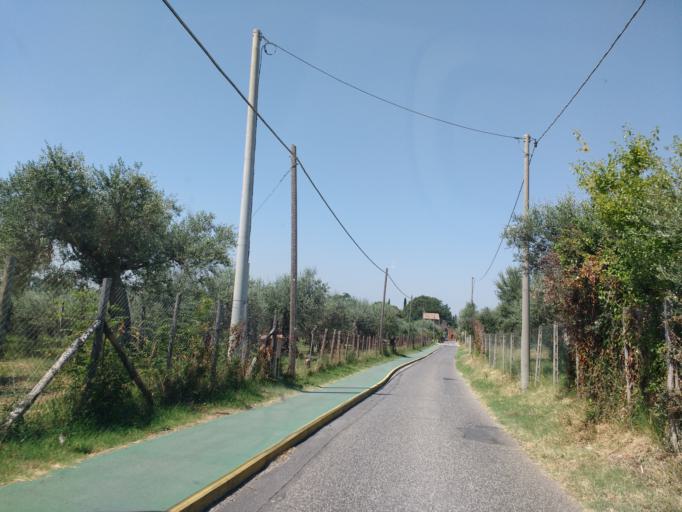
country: IT
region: Latium
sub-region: Citta metropolitana di Roma Capitale
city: Villa Adriana
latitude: 41.9477
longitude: 12.7834
